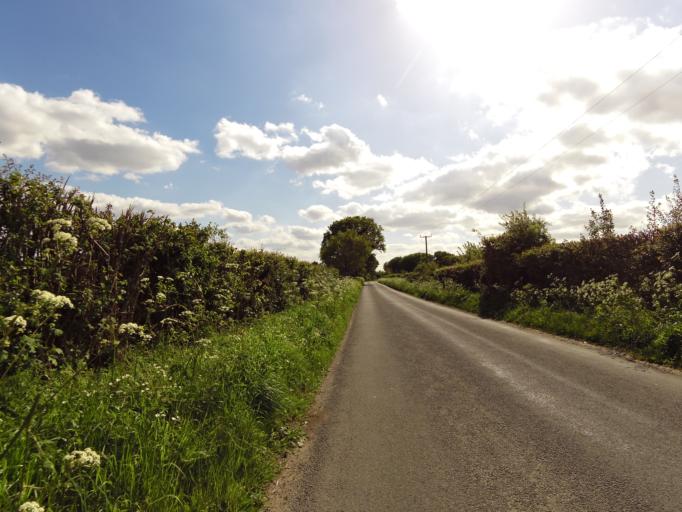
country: GB
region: England
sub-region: Suffolk
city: Kessingland
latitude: 52.4419
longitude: 1.6706
